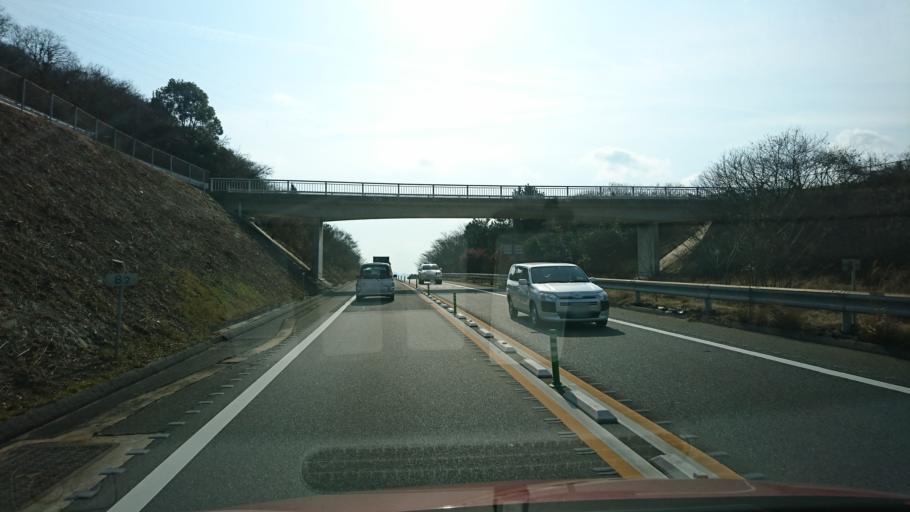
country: JP
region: Hiroshima
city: Onomichi
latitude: 34.3670
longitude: 133.1912
